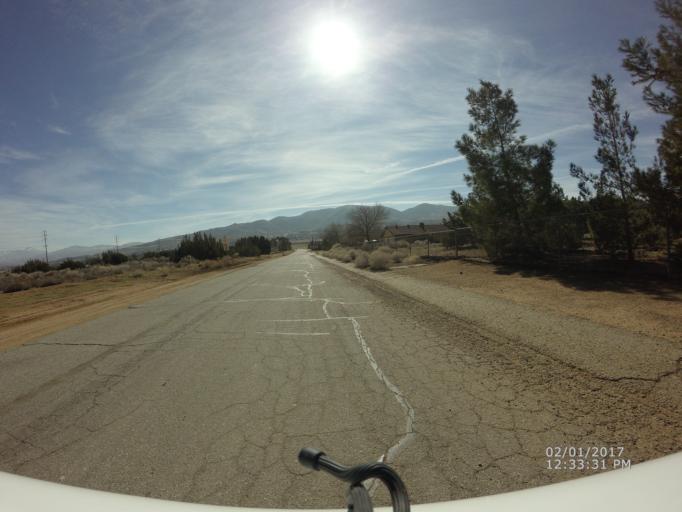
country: US
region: California
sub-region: Los Angeles County
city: Desert View Highlands
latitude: 34.5609
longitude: -118.1428
